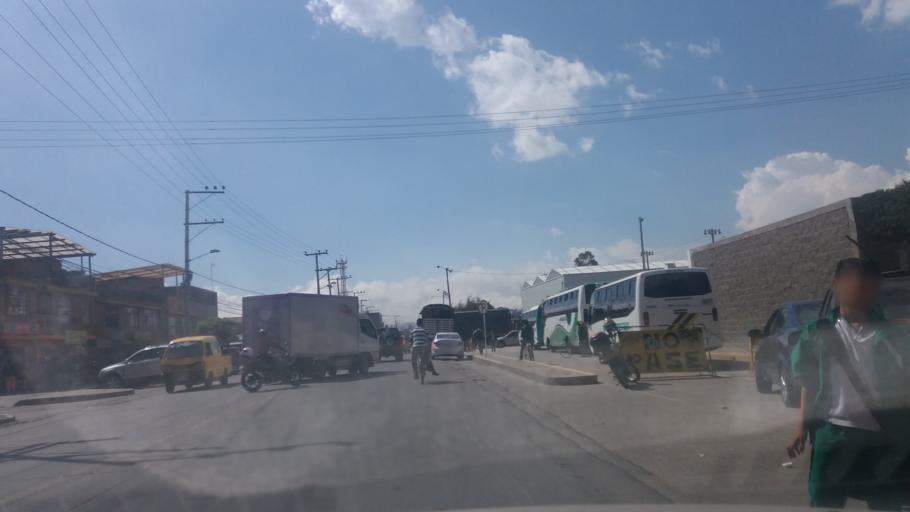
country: CO
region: Cundinamarca
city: Madrid
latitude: 4.7357
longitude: -74.2705
